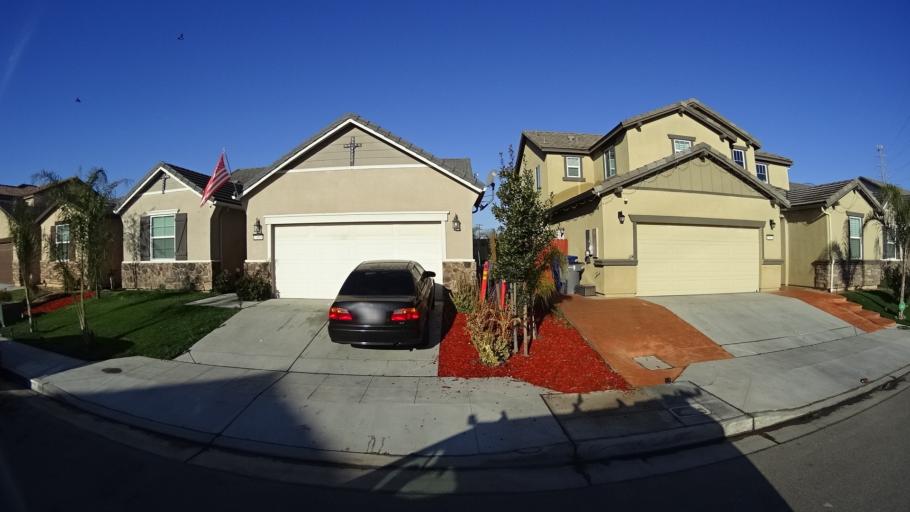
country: US
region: California
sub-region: Fresno County
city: Biola
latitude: 36.8384
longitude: -119.9147
